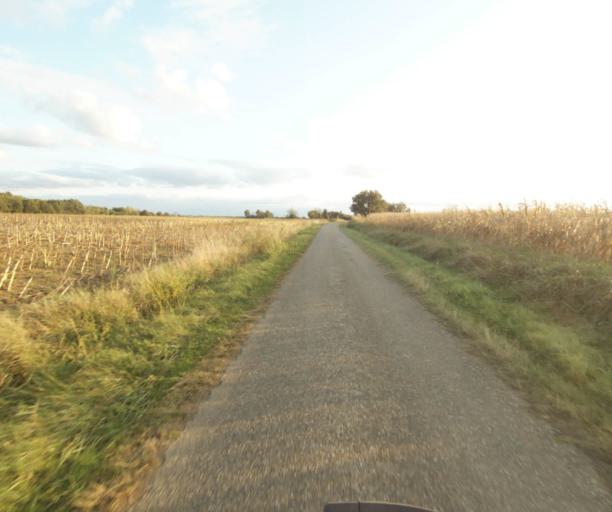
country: FR
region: Midi-Pyrenees
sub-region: Departement du Tarn-et-Garonne
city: Verdun-sur-Garonne
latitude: 43.8280
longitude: 1.1606
